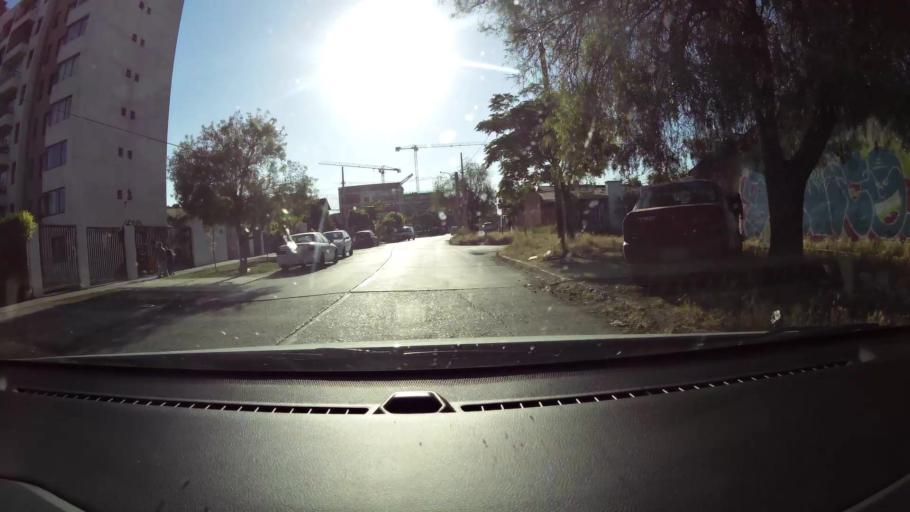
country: CL
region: Santiago Metropolitan
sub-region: Provincia de Santiago
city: La Pintana
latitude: -33.5374
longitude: -70.6695
